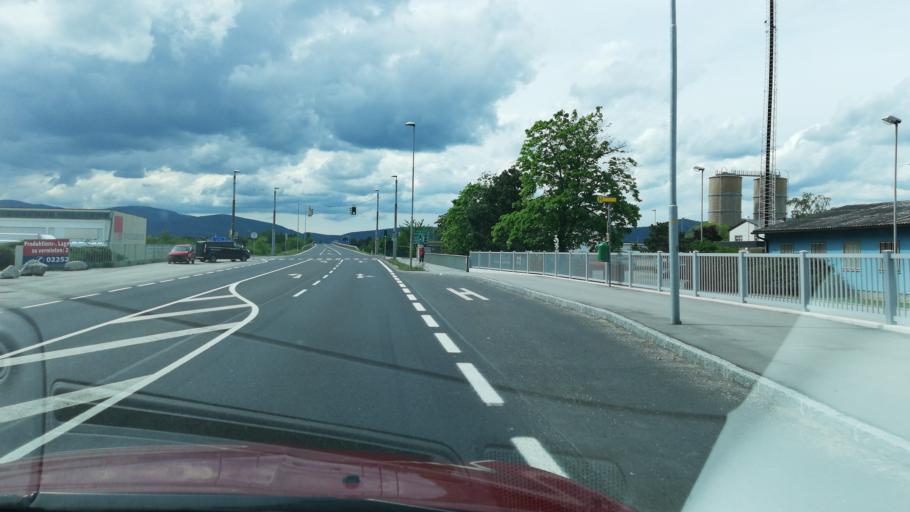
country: AT
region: Lower Austria
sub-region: Politischer Bezirk Baden
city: Traiskirchen
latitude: 47.9876
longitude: 16.2867
